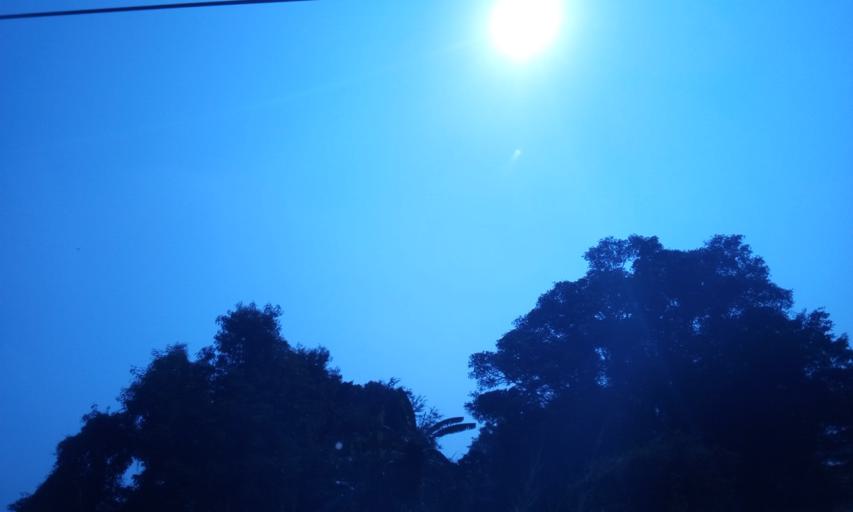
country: TH
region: Pathum Thani
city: Thanyaburi
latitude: 13.9763
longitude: 100.7061
